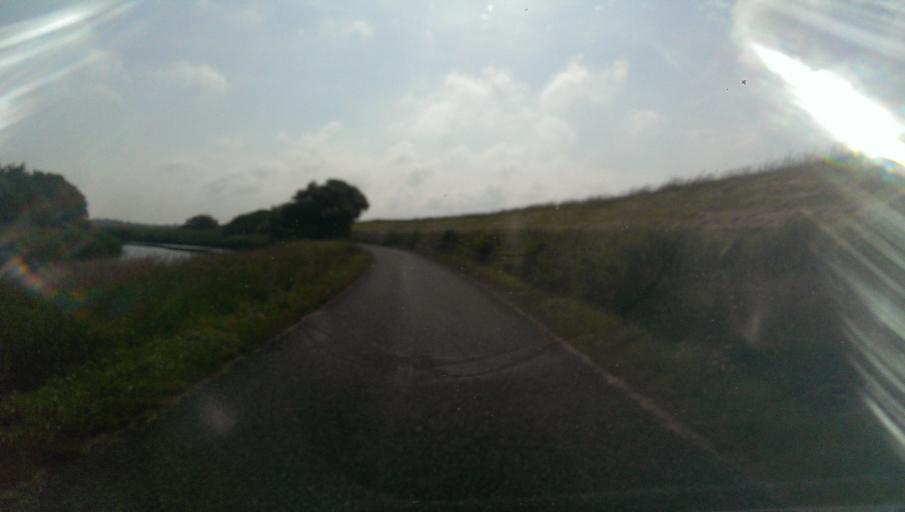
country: DK
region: South Denmark
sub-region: Esbjerg Kommune
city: Tjaereborg
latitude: 55.4331
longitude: 8.6093
